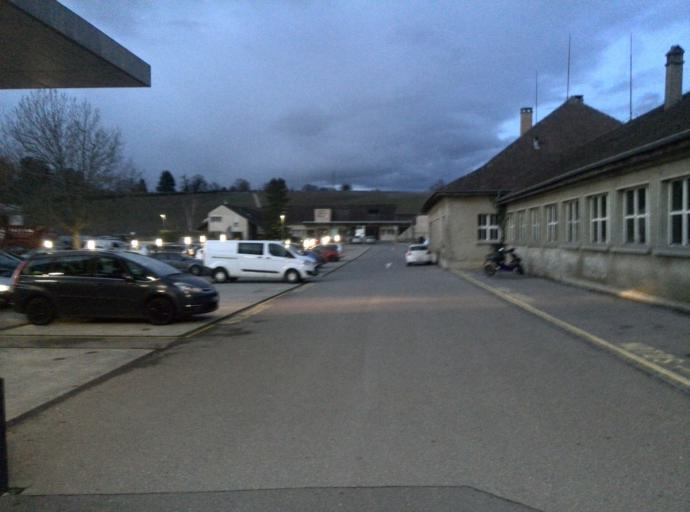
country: CH
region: Vaud
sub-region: Morges District
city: Morges
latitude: 46.5177
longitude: 6.4870
